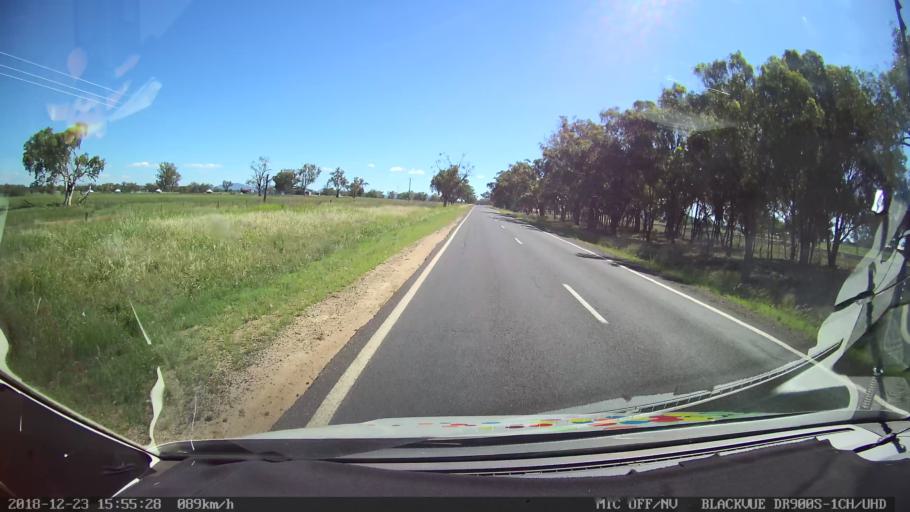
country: AU
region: New South Wales
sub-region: Tamworth Municipality
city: Phillip
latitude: -31.1557
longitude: 150.8681
